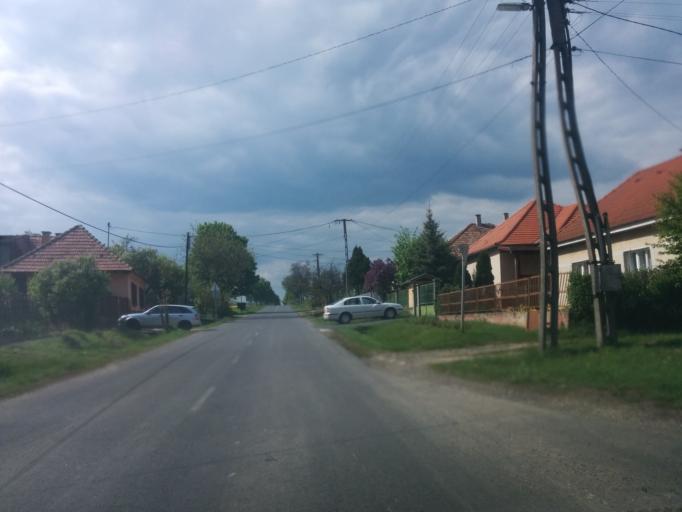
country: HU
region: Nograd
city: Romhany
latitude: 47.8451
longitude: 19.2871
